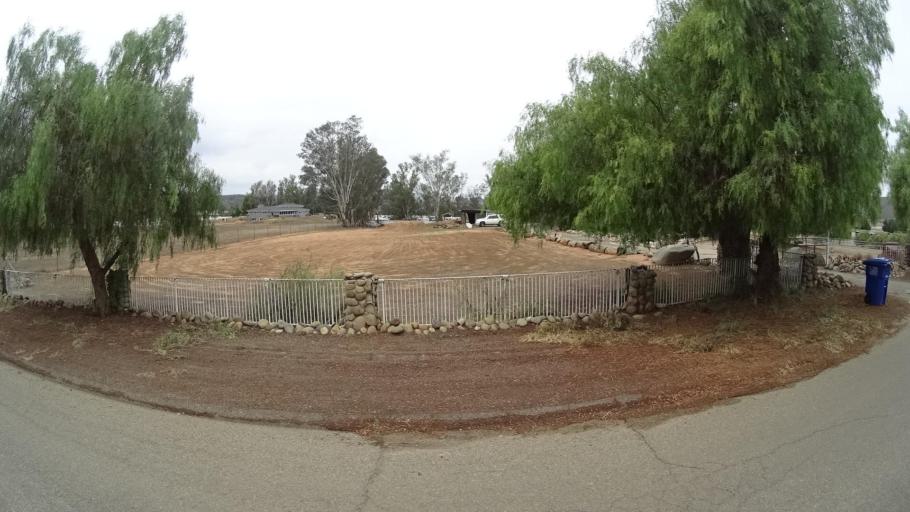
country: US
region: California
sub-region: San Diego County
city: Ramona
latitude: 33.0706
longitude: -116.8718
